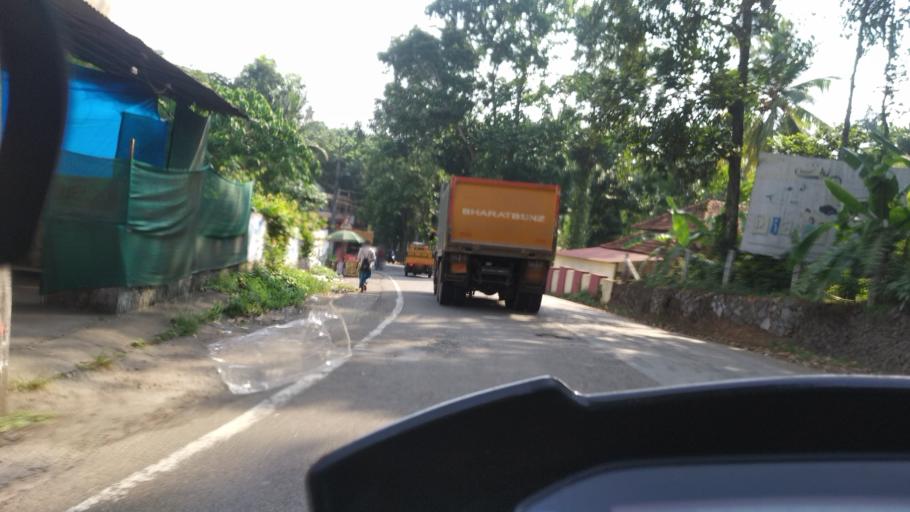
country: IN
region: Kerala
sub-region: Ernakulam
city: Piravam
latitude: 9.8737
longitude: 76.4932
